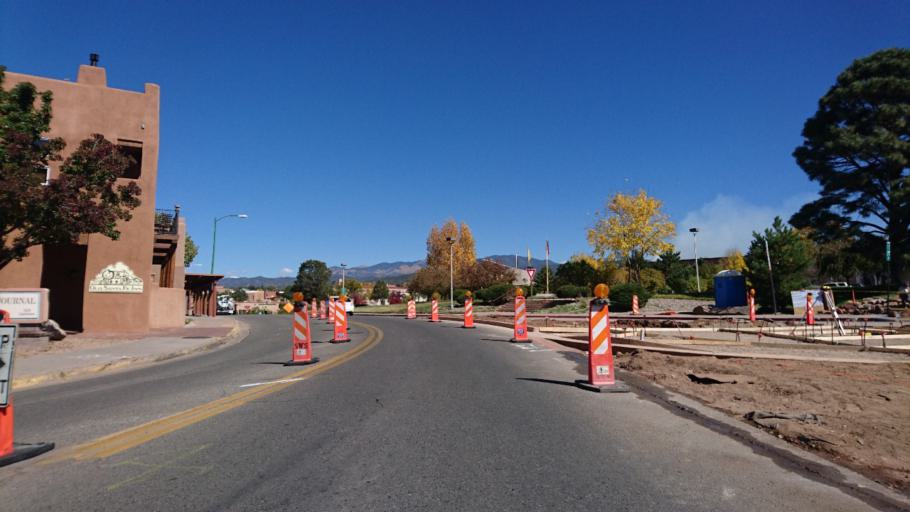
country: US
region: New Mexico
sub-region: Santa Fe County
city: Santa Fe
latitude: 35.6843
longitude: -105.9426
